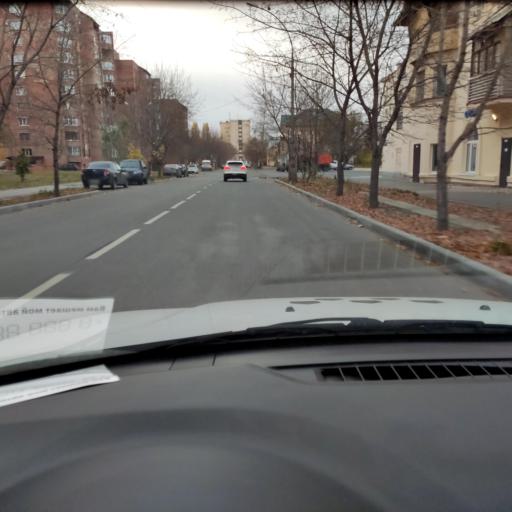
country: RU
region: Samara
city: Tol'yatti
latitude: 53.5034
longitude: 49.3938
